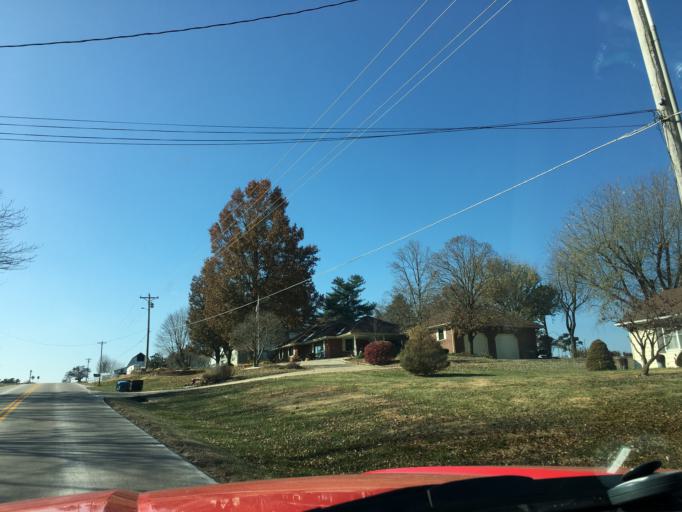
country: US
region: Missouri
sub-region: Cole County
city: Wardsville
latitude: 38.4874
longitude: -92.1804
